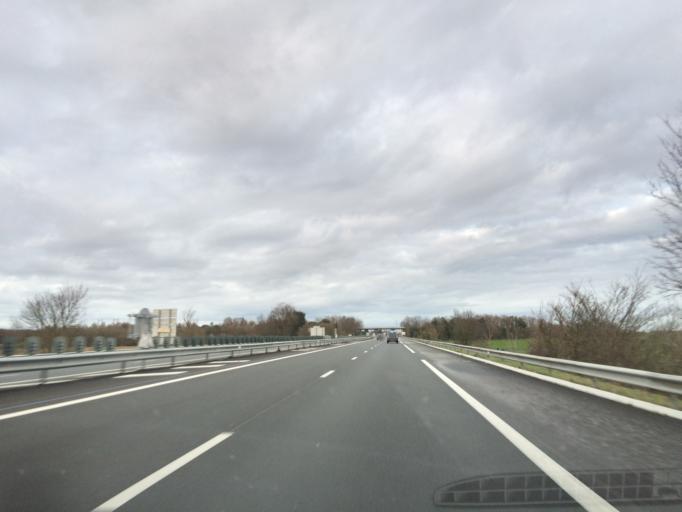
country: FR
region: Poitou-Charentes
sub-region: Departement des Deux-Sevres
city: Fors
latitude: 46.2291
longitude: -0.4434
